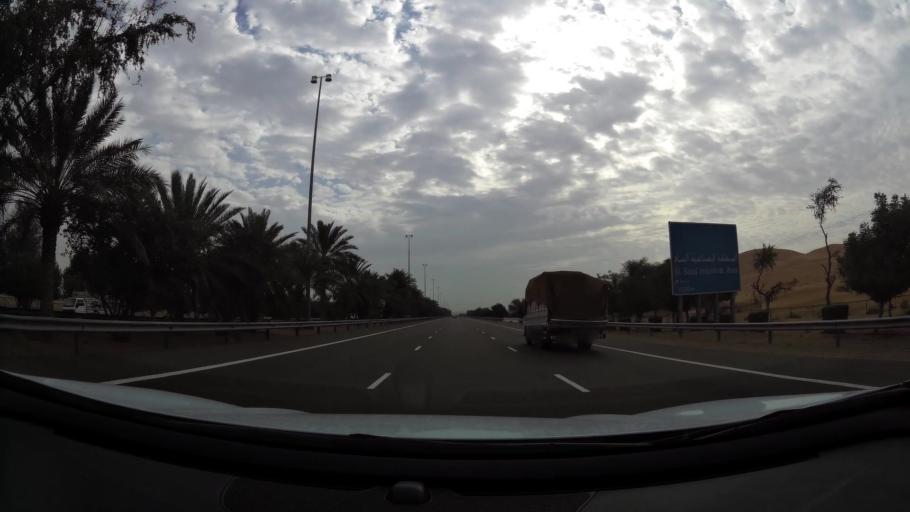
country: AE
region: Abu Dhabi
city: Al Ain
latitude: 24.2116
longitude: 55.4990
